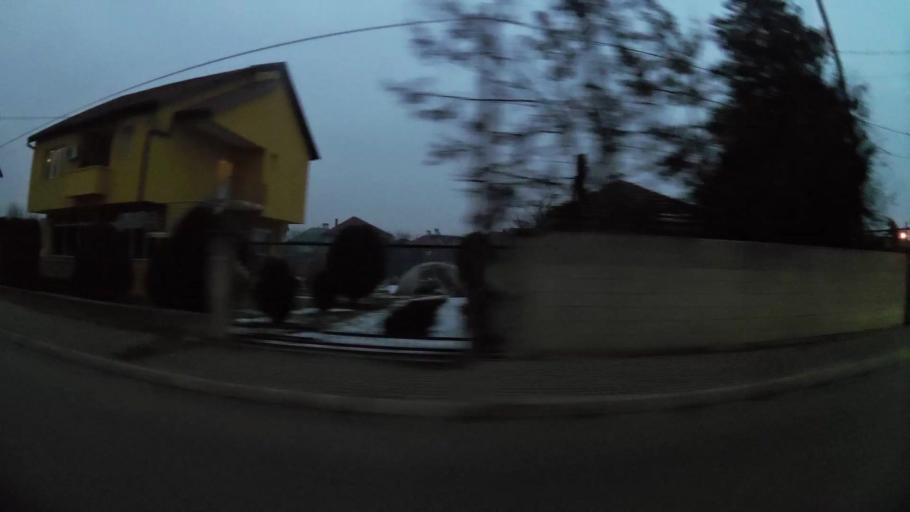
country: MK
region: Kisela Voda
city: Kisela Voda
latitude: 41.9687
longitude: 21.4879
